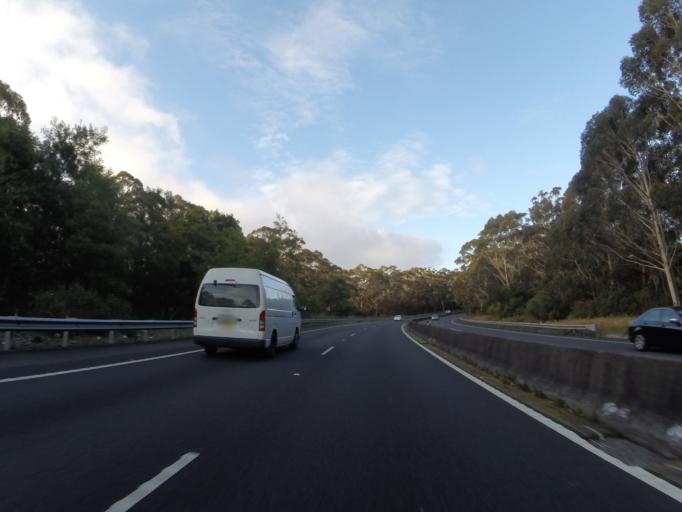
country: AU
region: New South Wales
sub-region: Wollongong
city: Bulli
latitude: -34.3252
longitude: 150.8775
